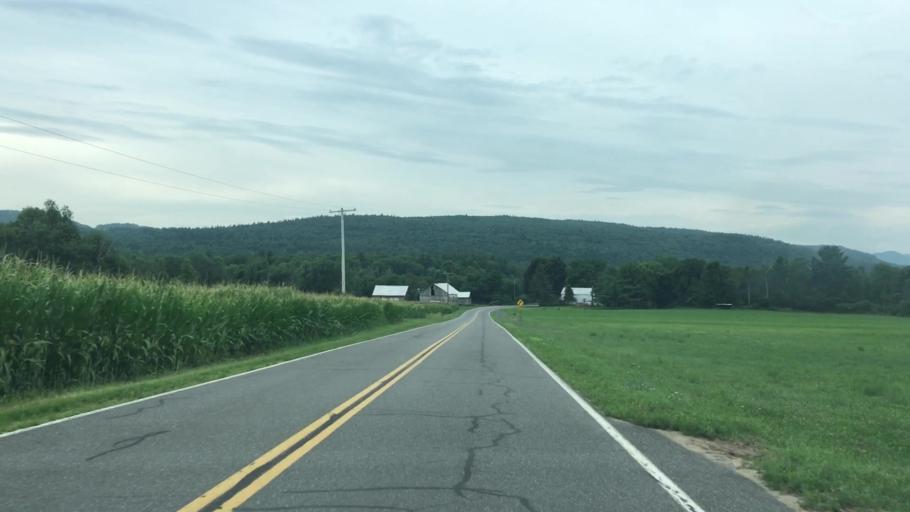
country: US
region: New York
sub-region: Clinton County
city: Peru
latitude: 44.5321
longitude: -73.5737
